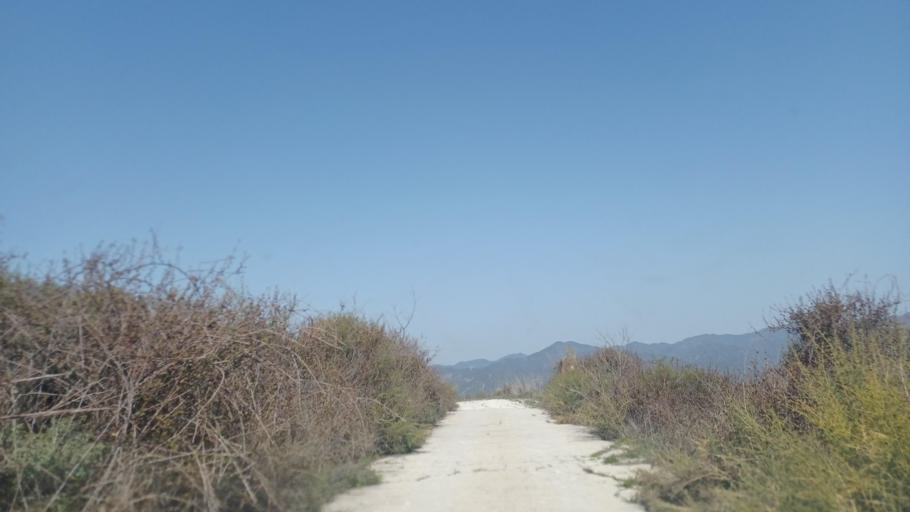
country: CY
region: Limassol
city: Pachna
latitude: 34.8784
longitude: 32.7078
